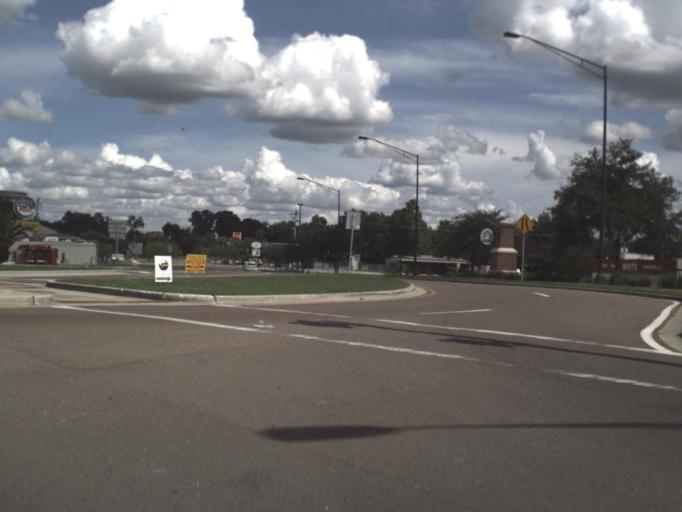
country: US
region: Florida
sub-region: Polk County
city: Bartow
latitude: 27.8965
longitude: -81.8536
